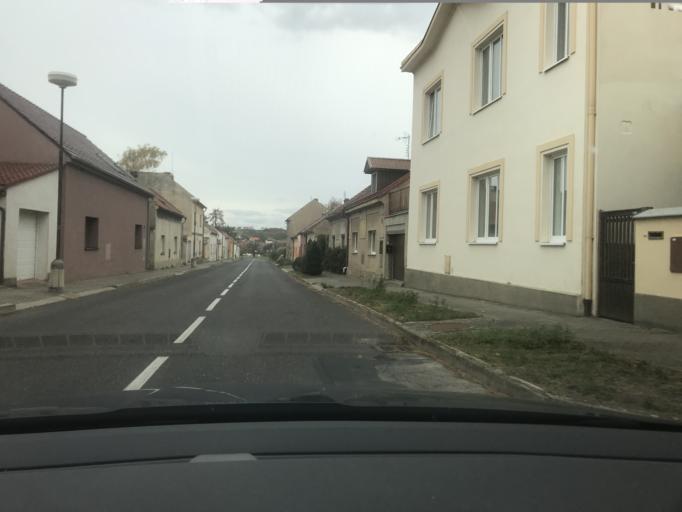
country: CZ
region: Ustecky
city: Trebenice
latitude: 50.4724
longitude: 13.9976
